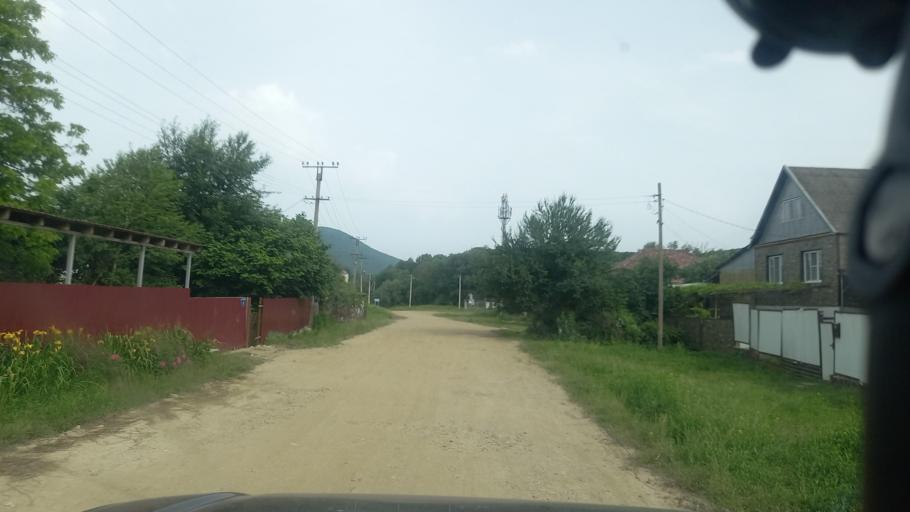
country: RU
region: Krasnodarskiy
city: Goryachiy Klyuch
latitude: 44.6055
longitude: 39.0214
